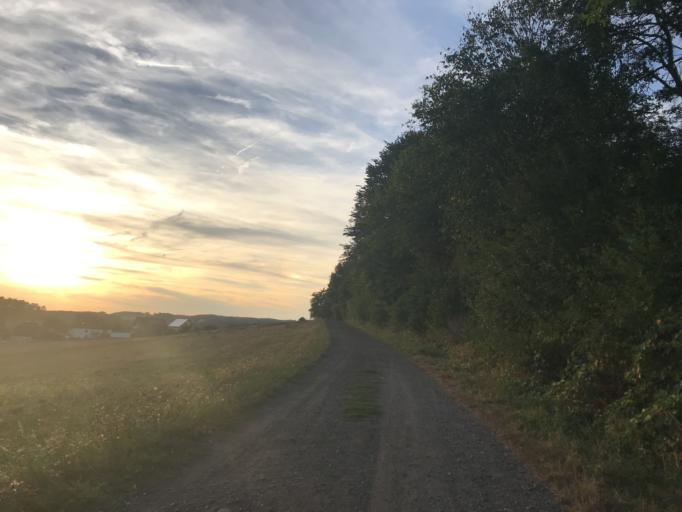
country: DE
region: Bavaria
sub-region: Upper Palatinate
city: Auerbach
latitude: 49.7203
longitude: 11.6237
